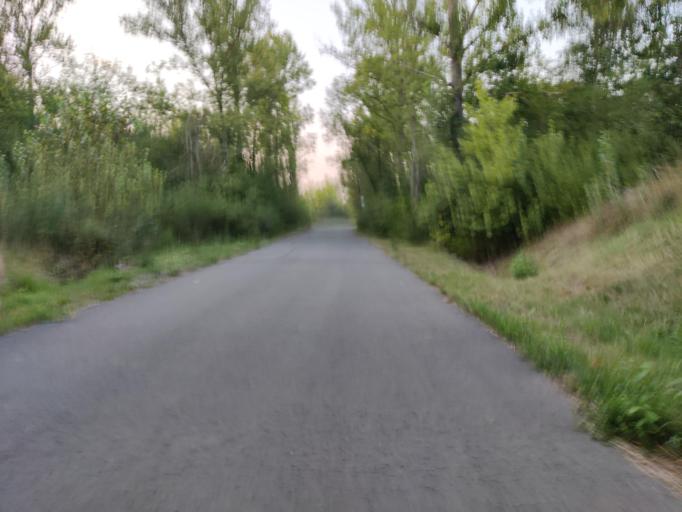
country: DE
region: Saxony
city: Zschortau
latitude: 51.4465
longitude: 12.3207
